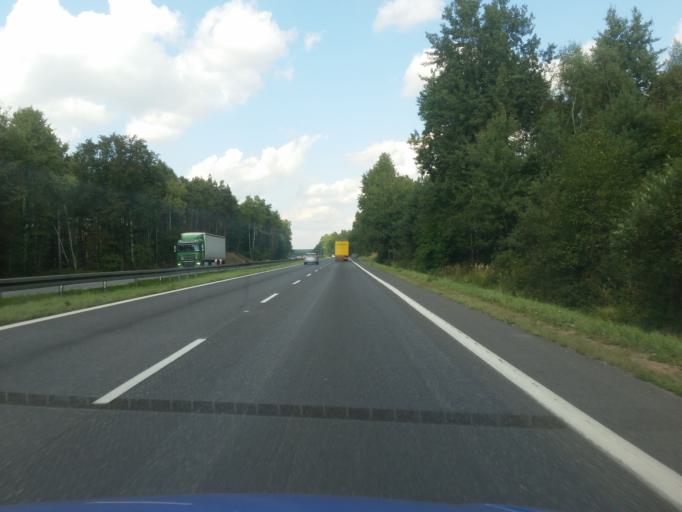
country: PL
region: Silesian Voivodeship
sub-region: Powiat bedzinski
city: Siewierz
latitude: 50.5232
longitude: 19.1930
